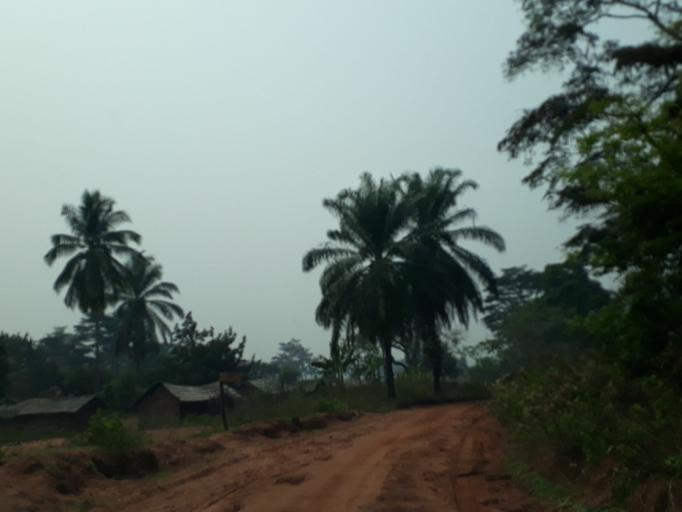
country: CD
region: Kasai-Occidental
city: Tshikapa
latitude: -6.1609
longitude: 20.4215
